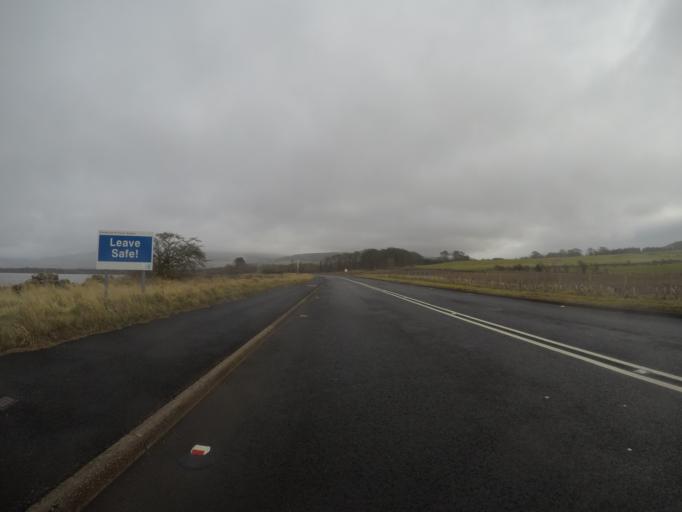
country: GB
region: Scotland
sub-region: North Ayrshire
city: Millport
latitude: 55.7272
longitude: -4.8902
